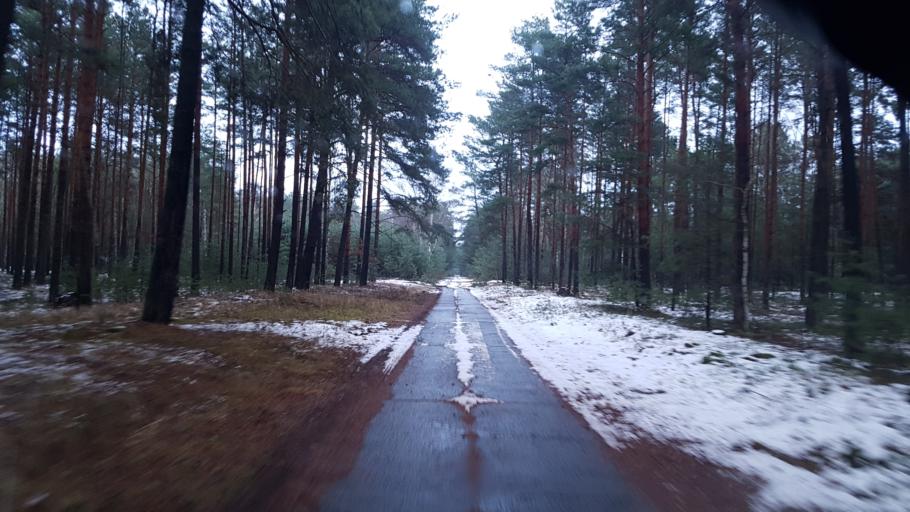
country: DE
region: Brandenburg
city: Janschwalde
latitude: 51.8838
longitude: 14.5389
